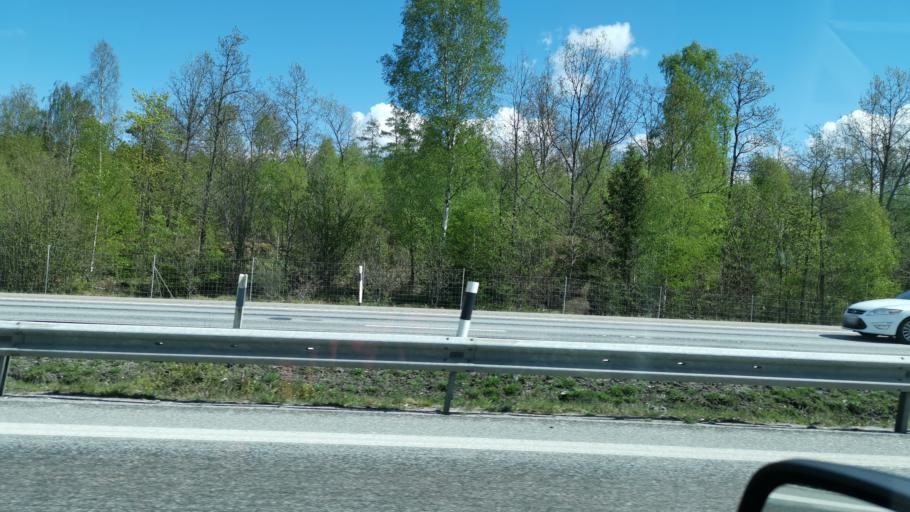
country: SE
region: Vaestra Goetaland
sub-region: Uddevalla Kommun
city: Ljungskile
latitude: 58.1922
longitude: 11.9086
